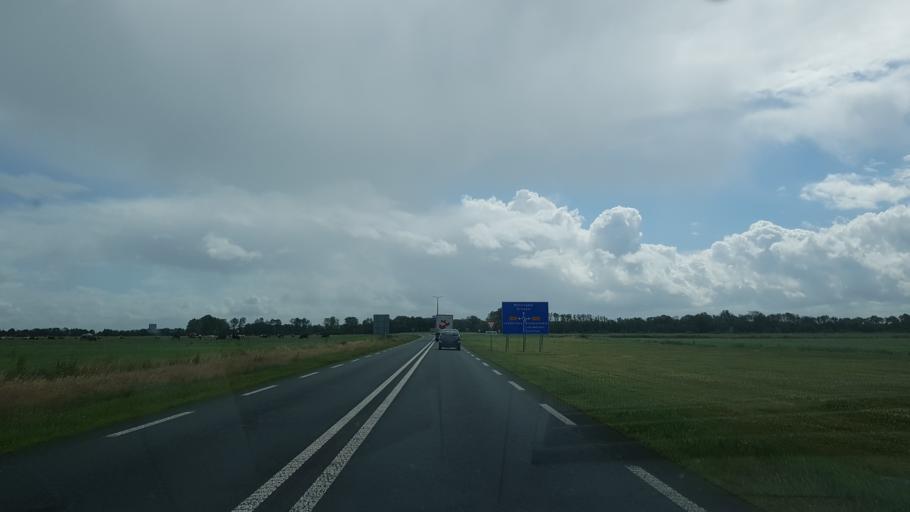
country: NL
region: Friesland
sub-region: Gemeente Dantumadiel
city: Walterswald
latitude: 53.3111
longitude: 6.0161
